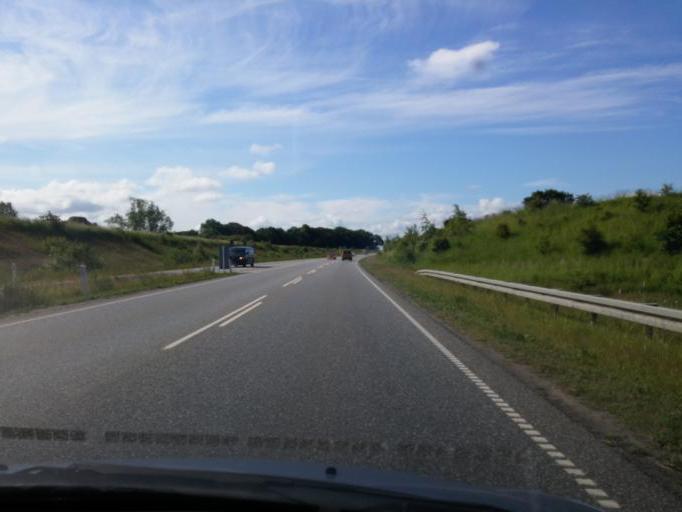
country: DK
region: South Denmark
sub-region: Odense Kommune
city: Neder Holluf
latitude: 55.3851
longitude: 10.4796
